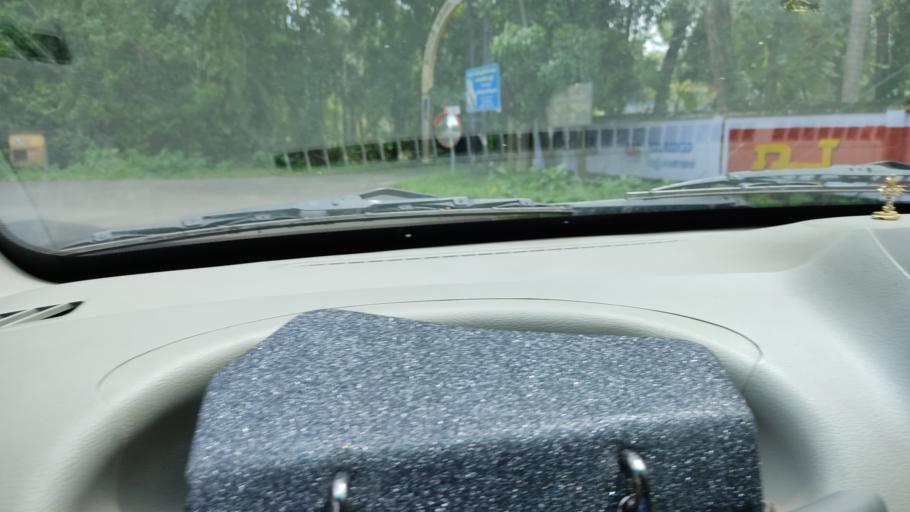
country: IN
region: Kerala
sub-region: Pattanamtitta
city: Tiruvalla
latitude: 9.3306
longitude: 76.5242
